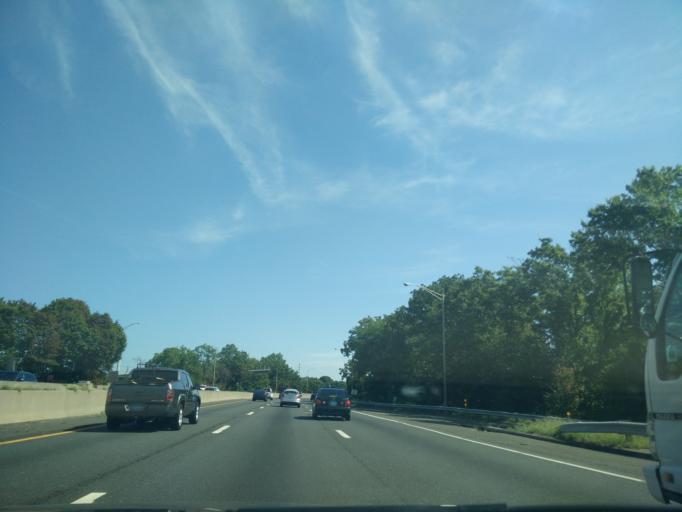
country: US
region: Connecticut
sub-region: Fairfield County
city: Stratford
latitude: 41.1914
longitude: -73.1333
